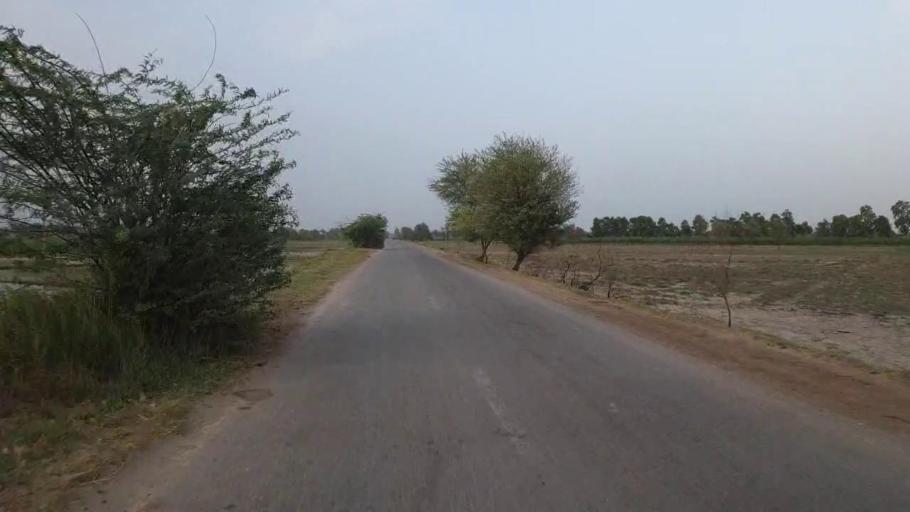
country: PK
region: Sindh
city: Daur
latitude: 26.4255
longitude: 68.2574
